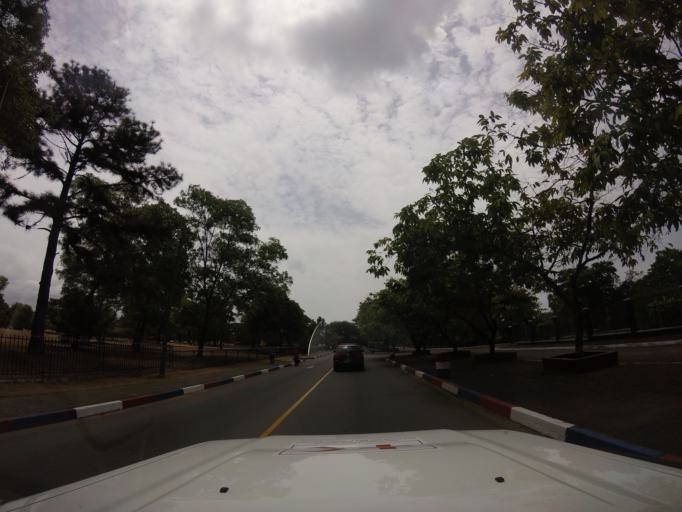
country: LR
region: Montserrado
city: Monrovia
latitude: 6.3007
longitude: -10.7968
